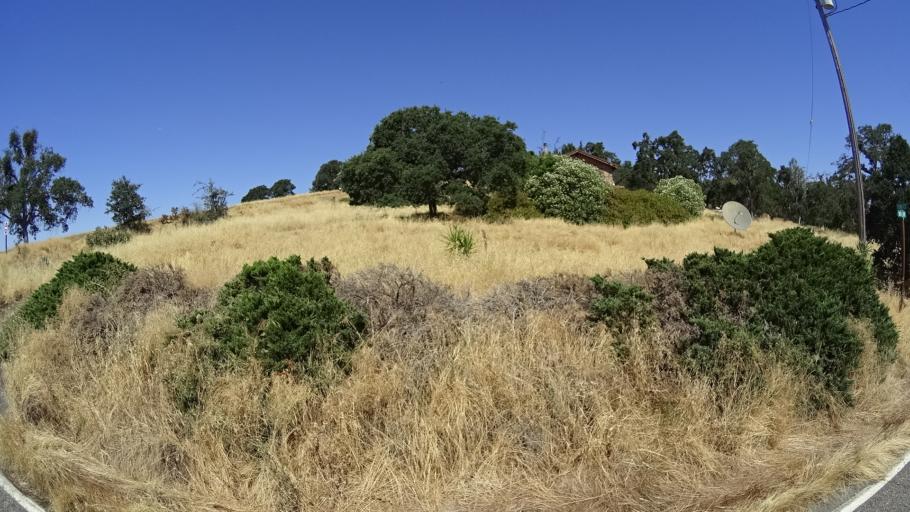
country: US
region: California
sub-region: Calaveras County
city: Copperopolis
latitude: 37.9240
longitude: -120.6282
